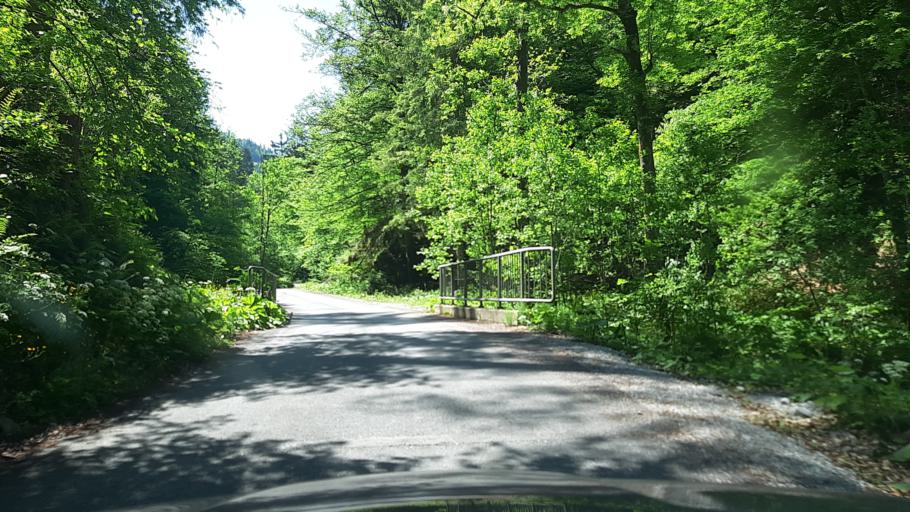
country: SI
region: Skofja Loka
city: Skofja Loka
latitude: 46.1191
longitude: 14.2703
